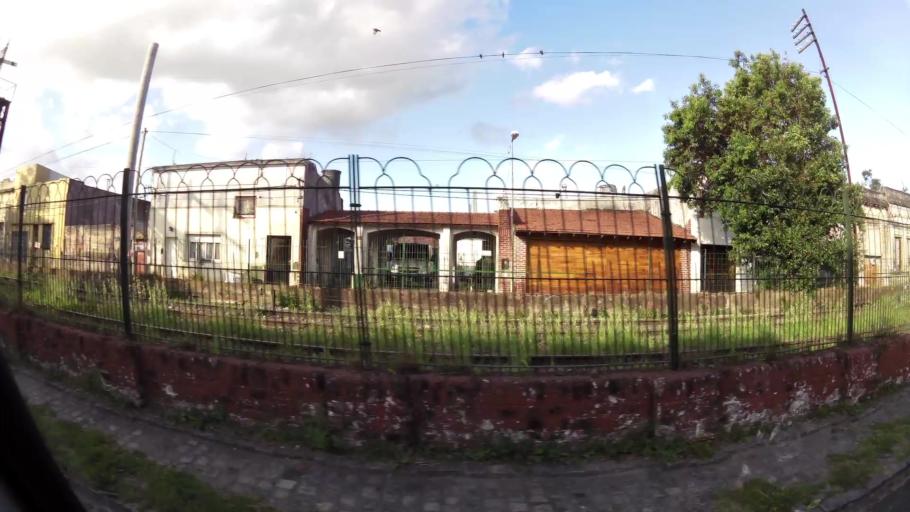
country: AR
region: Buenos Aires
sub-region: Partido de La Plata
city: La Plata
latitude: -34.8931
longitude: -57.9654
